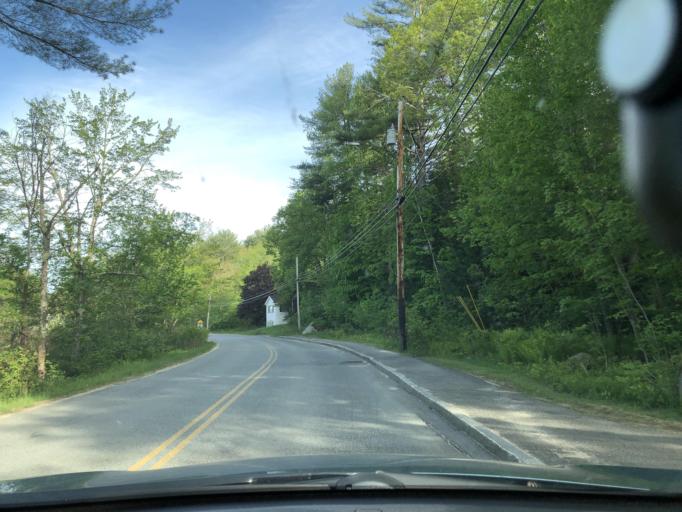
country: US
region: New Hampshire
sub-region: Merrimack County
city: Wilmot
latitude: 43.4184
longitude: -71.9338
